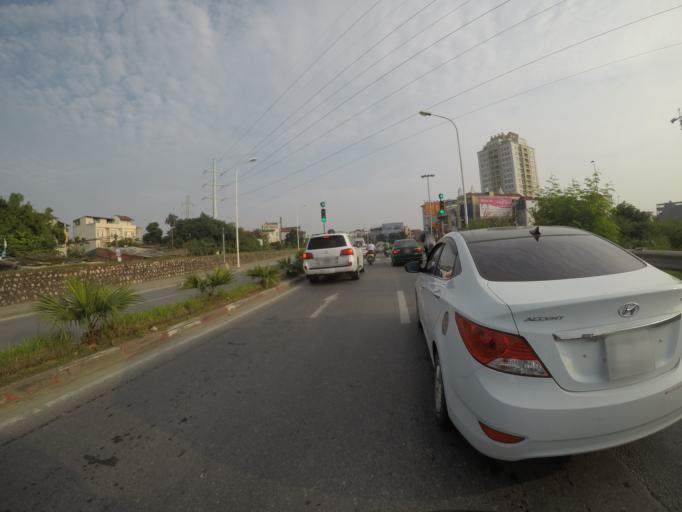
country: VN
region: Ha Noi
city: Tay Ho
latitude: 21.0827
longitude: 105.8172
